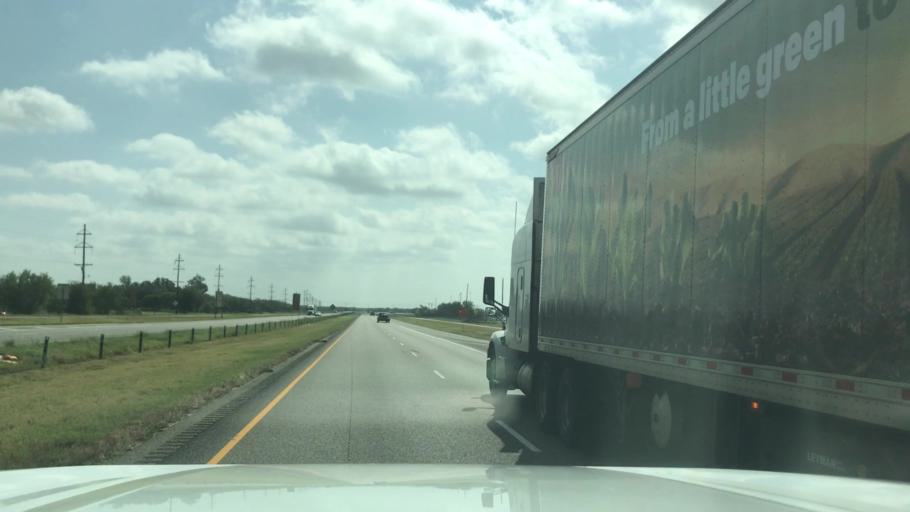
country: US
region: Texas
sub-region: Taylor County
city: Merkel
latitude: 32.4954
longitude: -100.1378
